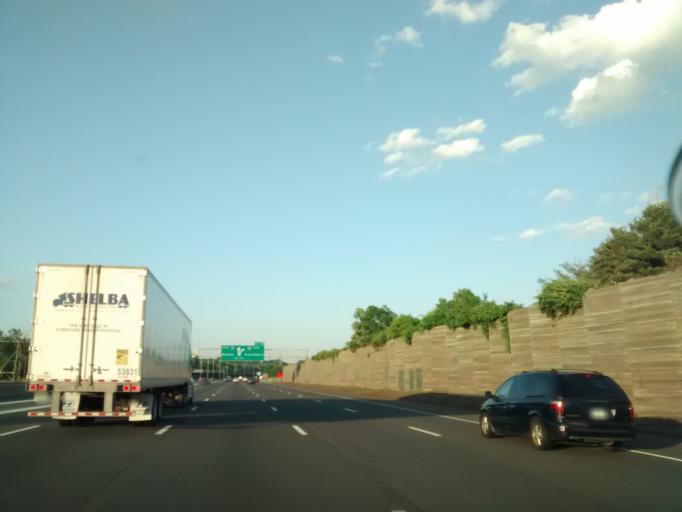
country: US
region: Connecticut
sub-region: Hartford County
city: East Hartford
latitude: 41.7688
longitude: -72.6129
